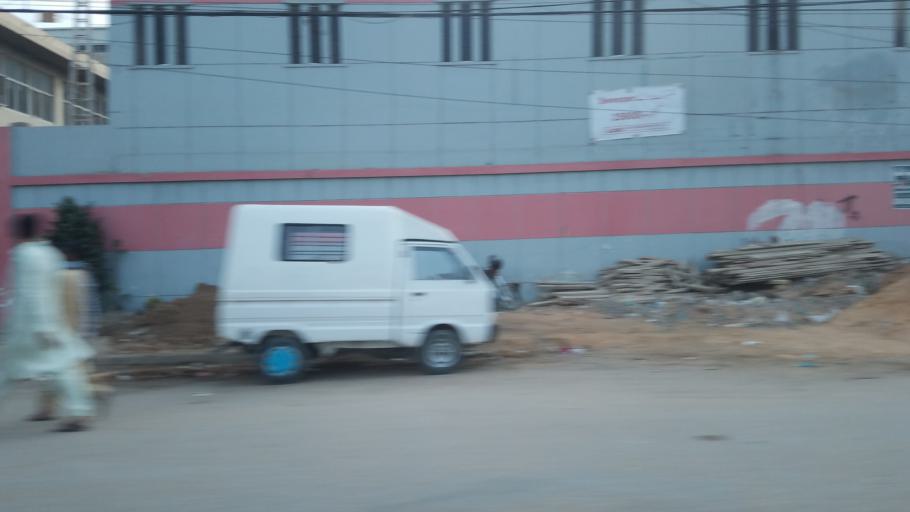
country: PK
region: Sindh
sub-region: Karachi District
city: Karachi
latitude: 24.9363
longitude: 67.0855
